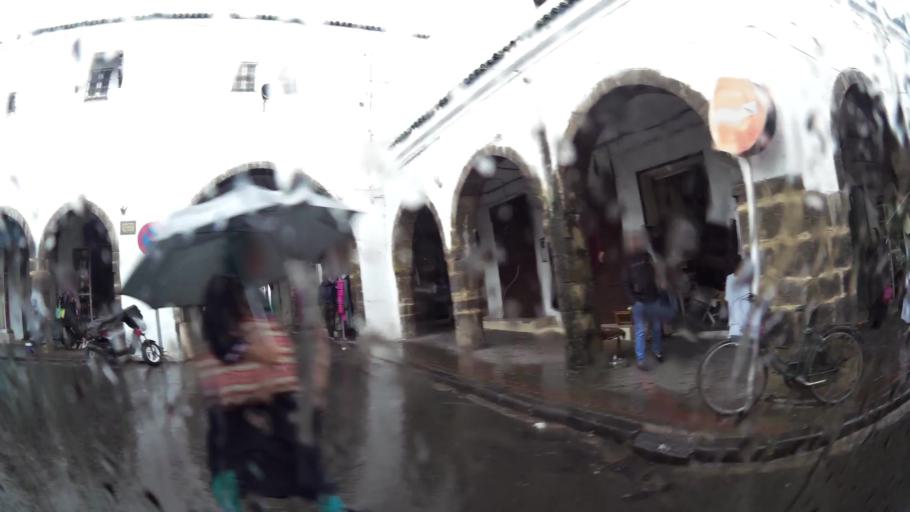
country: MA
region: Grand Casablanca
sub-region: Casablanca
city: Casablanca
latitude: 33.5776
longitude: -7.6049
